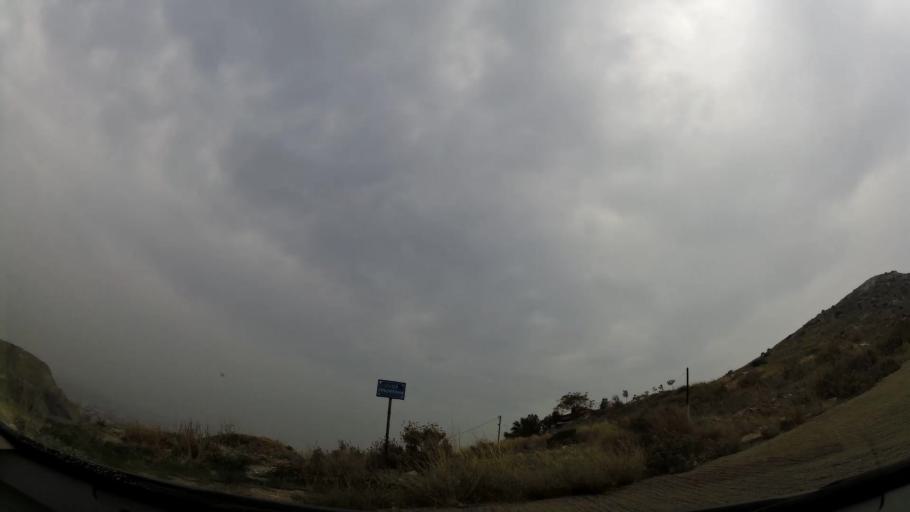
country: GR
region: Attica
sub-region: Nomos Piraios
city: Korydallos
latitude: 37.9941
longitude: 23.6398
